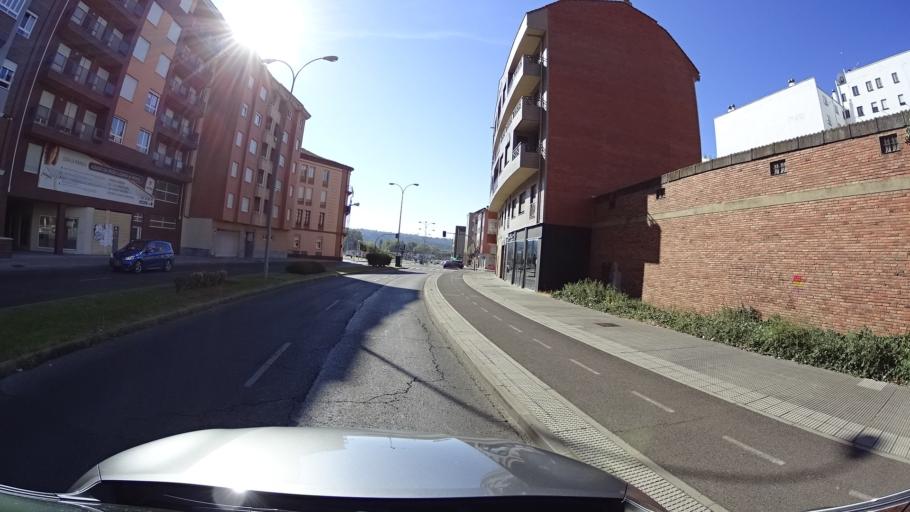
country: ES
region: Castille and Leon
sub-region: Provincia de Leon
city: Leon
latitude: 42.6036
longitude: -5.5608
